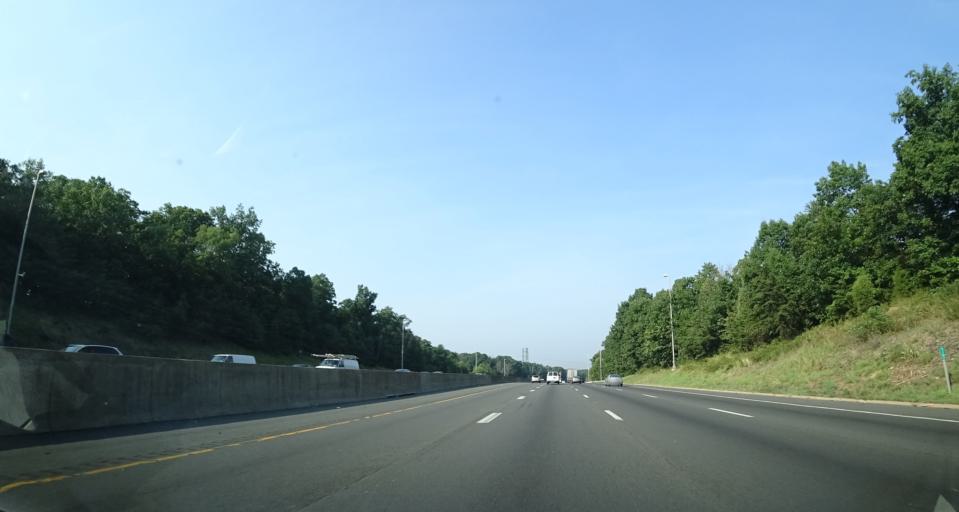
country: US
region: Virginia
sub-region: Fairfax County
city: Centreville
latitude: 38.8296
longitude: -77.4540
